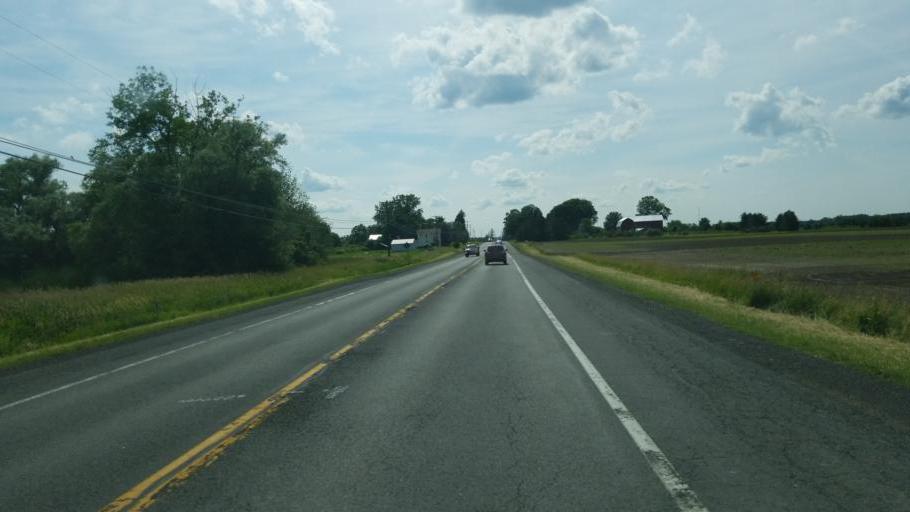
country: US
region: New York
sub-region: Ontario County
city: Clifton Springs
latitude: 42.8607
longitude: -77.1617
